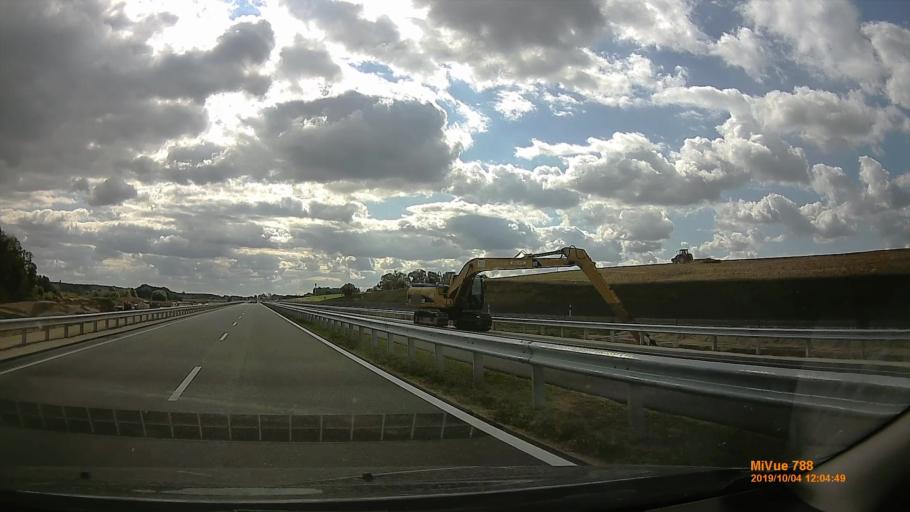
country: HU
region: Somogy
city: Karad
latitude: 46.5687
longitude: 17.8078
